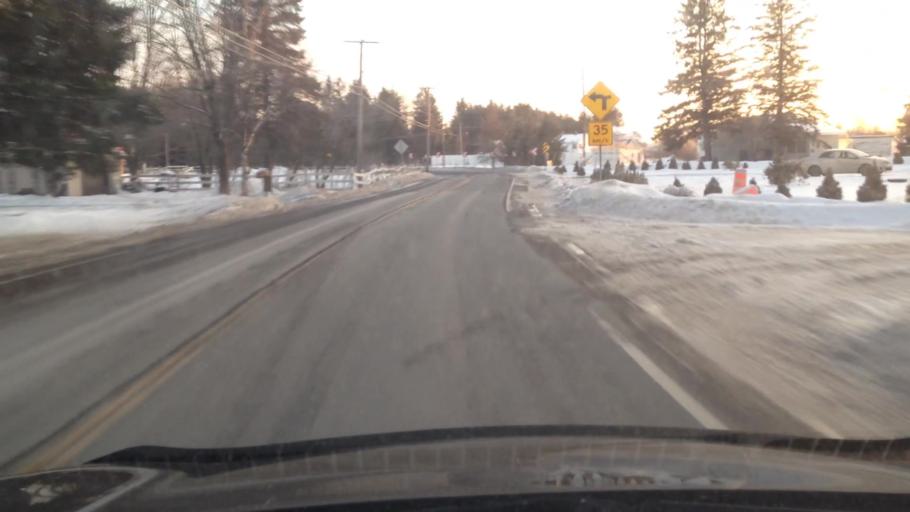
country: CA
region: Quebec
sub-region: Lanaudiere
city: Sainte-Julienne
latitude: 45.9170
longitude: -73.7385
